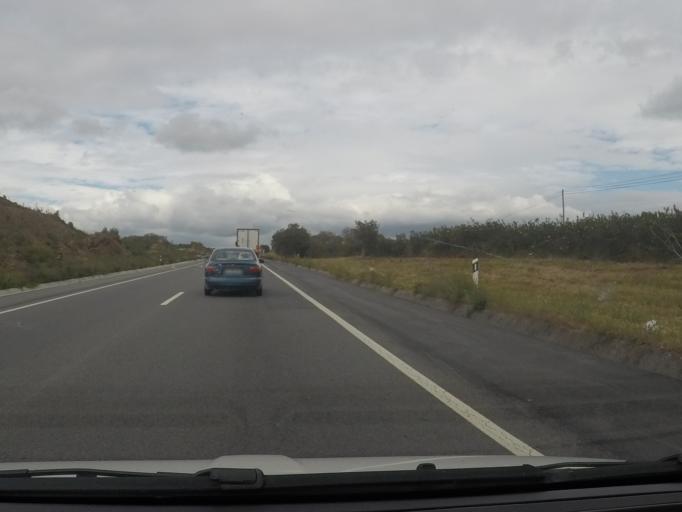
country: PT
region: Setubal
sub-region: Santiago do Cacem
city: Santiago do Cacem
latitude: 38.0681
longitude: -8.6869
